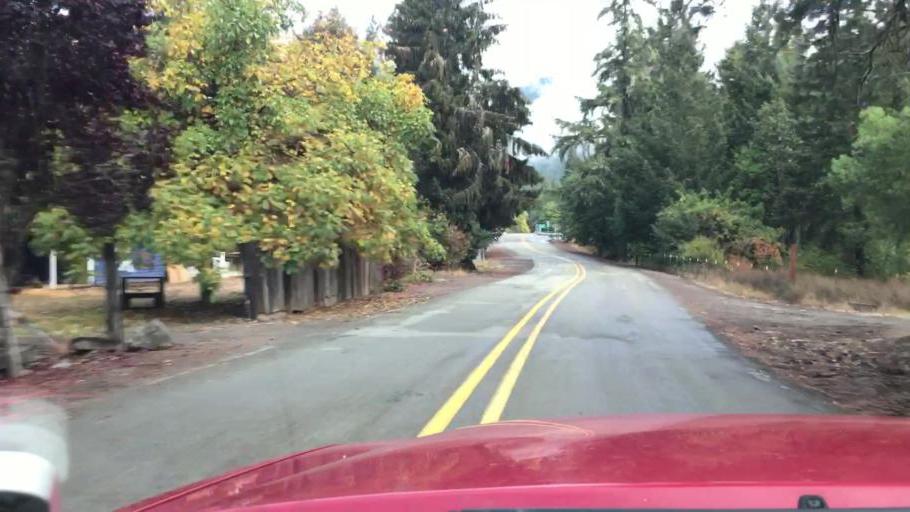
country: US
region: Oregon
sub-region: Douglas County
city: Canyonville
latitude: 42.7642
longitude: -123.3324
